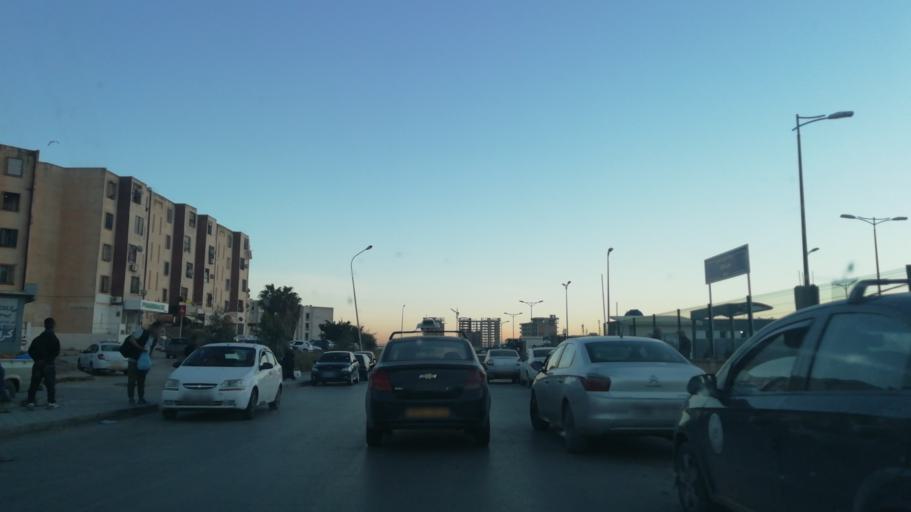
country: DZ
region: Oran
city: Bir el Djir
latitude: 35.7049
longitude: -0.5909
